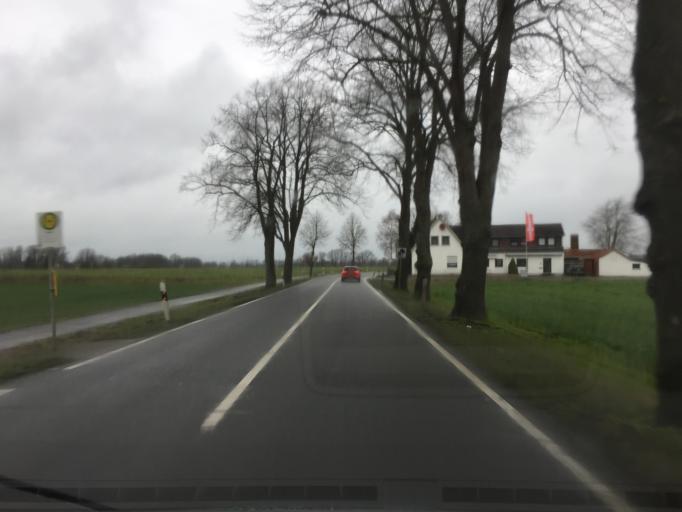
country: DE
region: Lower Saxony
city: Kirchseelte
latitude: 52.9697
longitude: 8.7088
